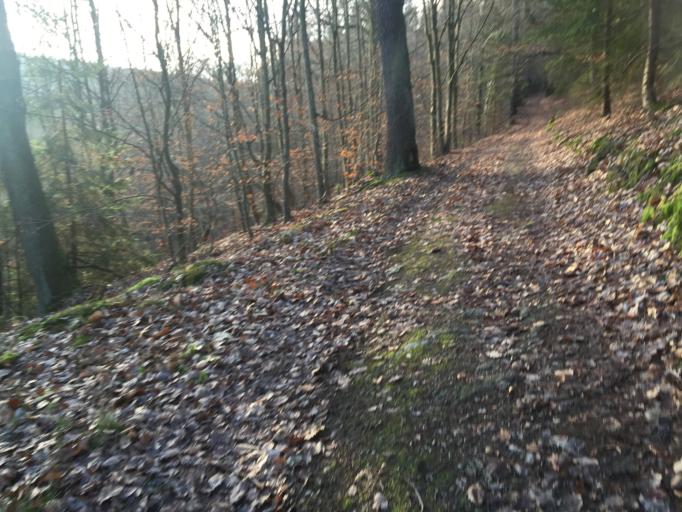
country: DE
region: Thuringia
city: Bad Blankenburg
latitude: 50.6613
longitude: 11.2527
